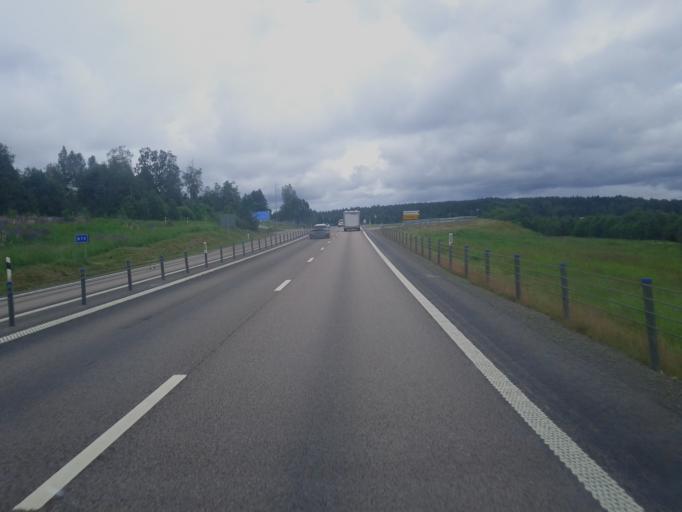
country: SE
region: Vaesternorrland
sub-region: Timra Kommun
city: Soraker
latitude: 62.5579
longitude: 17.6589
